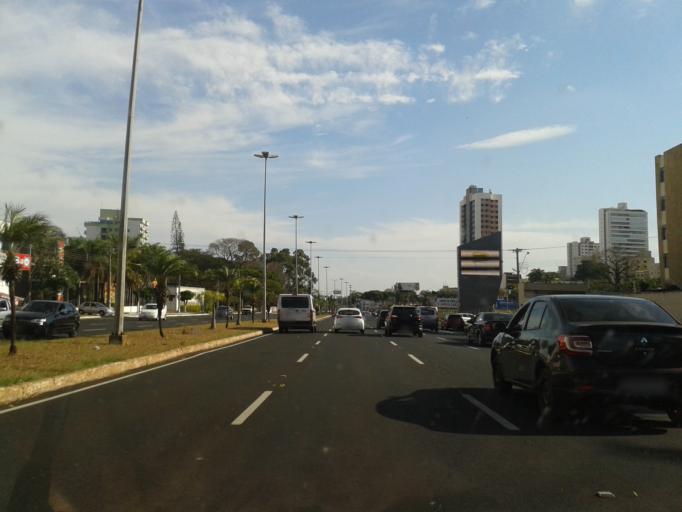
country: BR
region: Minas Gerais
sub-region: Uberlandia
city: Uberlandia
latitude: -18.9204
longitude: -48.2682
